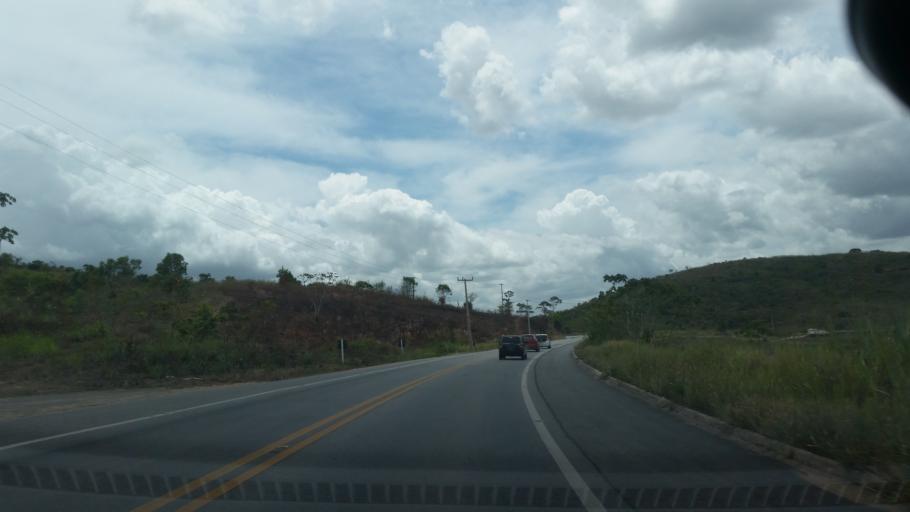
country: BR
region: Alagoas
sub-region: Uniao Dos Palmares
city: Uniao dos Palmares
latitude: -9.1985
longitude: -36.0315
